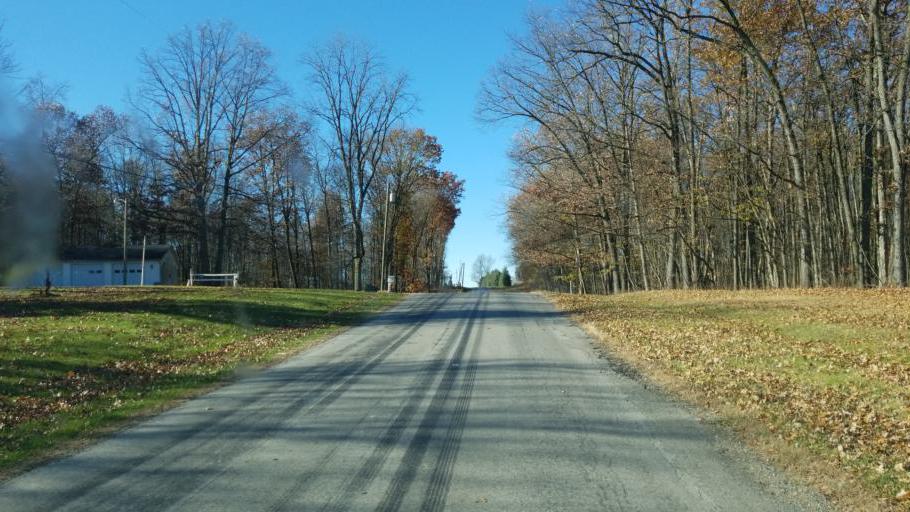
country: US
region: Ohio
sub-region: Huron County
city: Plymouth
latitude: 40.9696
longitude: -82.6552
